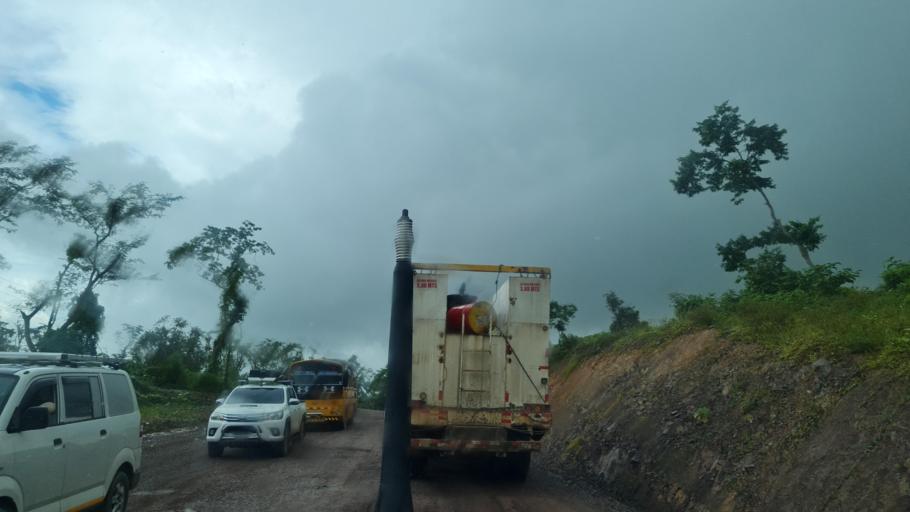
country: NI
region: Atlantico Norte (RAAN)
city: Siuna
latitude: 13.7020
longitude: -84.4448
